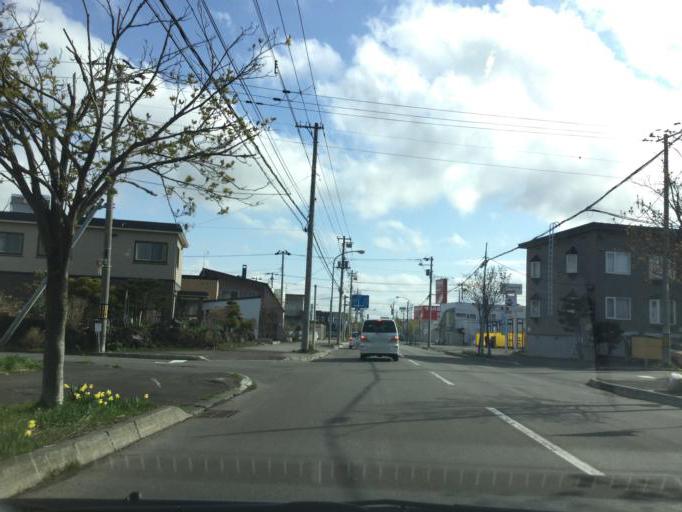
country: JP
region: Hokkaido
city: Ebetsu
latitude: 43.1101
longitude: 141.5282
